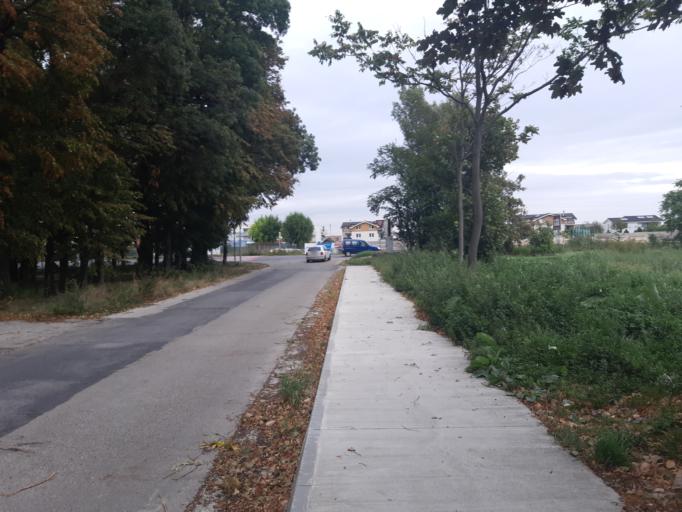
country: SK
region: Bratislavsky
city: Dunajska Luzna
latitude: 48.0915
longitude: 17.2458
